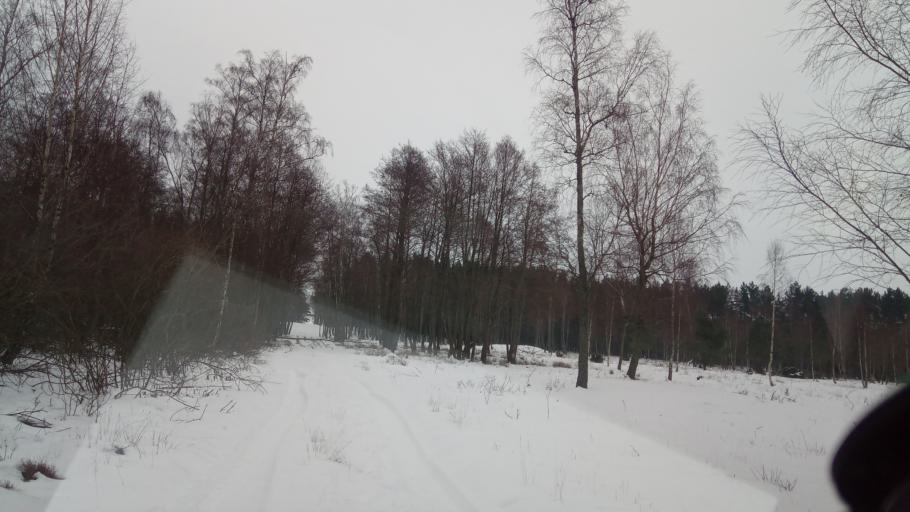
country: LT
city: Neringa
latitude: 55.4235
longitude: 21.1018
